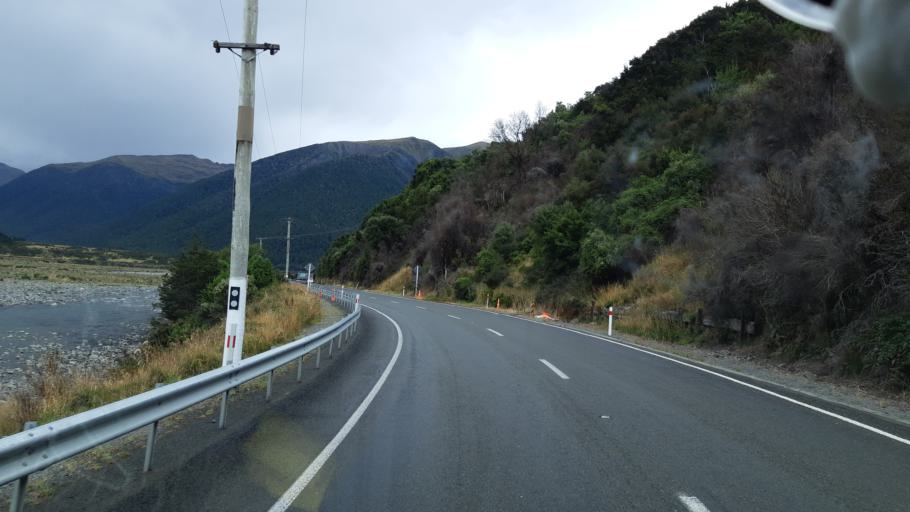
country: NZ
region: Canterbury
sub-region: Hurunui District
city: Amberley
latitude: -42.5627
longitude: 172.3534
